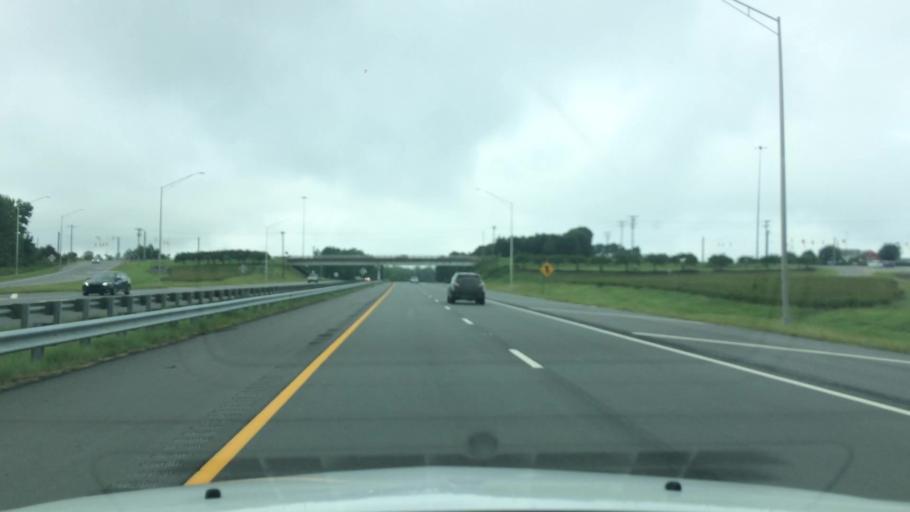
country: US
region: North Carolina
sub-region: Forsyth County
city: Lewisville
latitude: 36.0766
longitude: -80.3858
